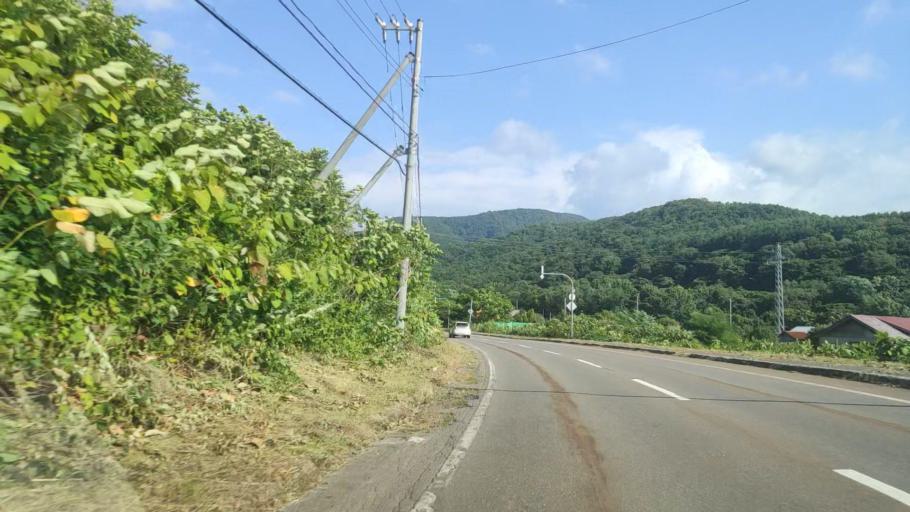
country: JP
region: Hokkaido
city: Ishikari
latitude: 43.5591
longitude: 141.3798
